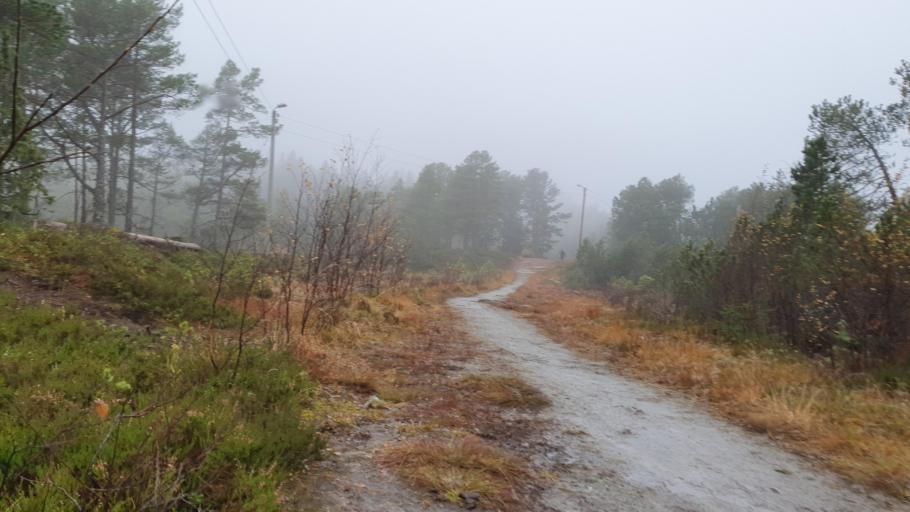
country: NO
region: Sor-Trondelag
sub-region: Trondheim
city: Trondheim
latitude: 63.4135
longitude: 10.3190
